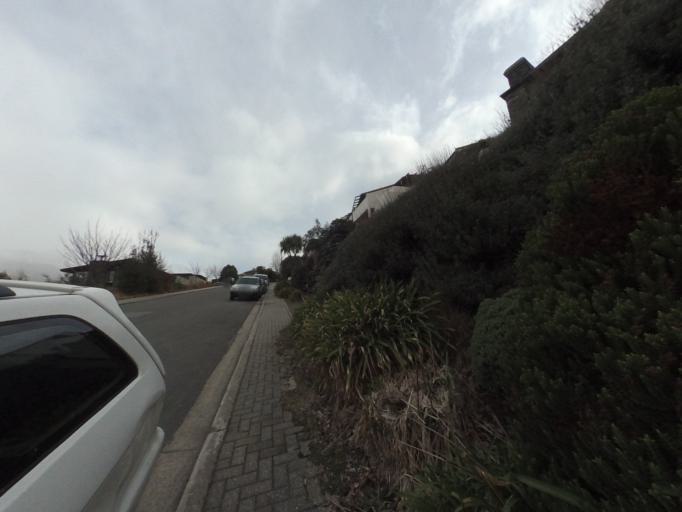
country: NZ
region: Otago
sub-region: Queenstown-Lakes District
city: Queenstown
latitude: -45.0396
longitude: 168.6366
